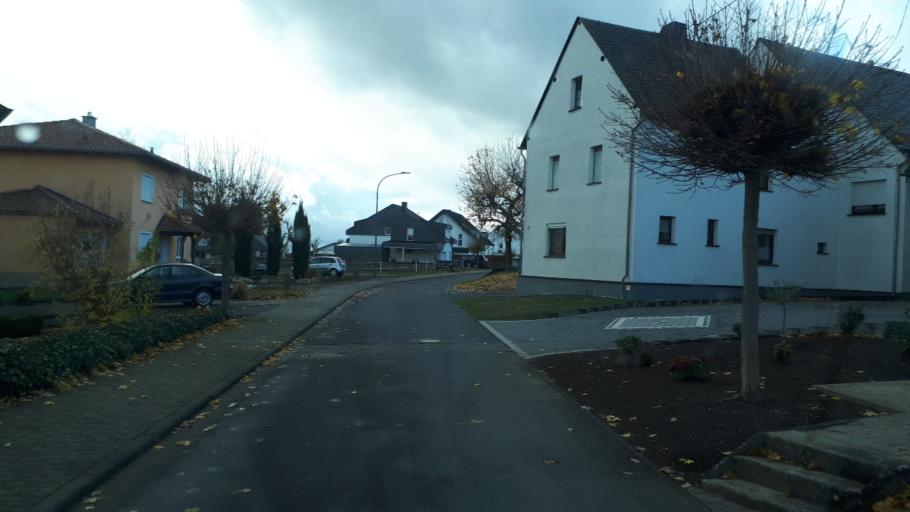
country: DE
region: Rheinland-Pfalz
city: Binningen
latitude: 50.2096
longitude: 7.2528
